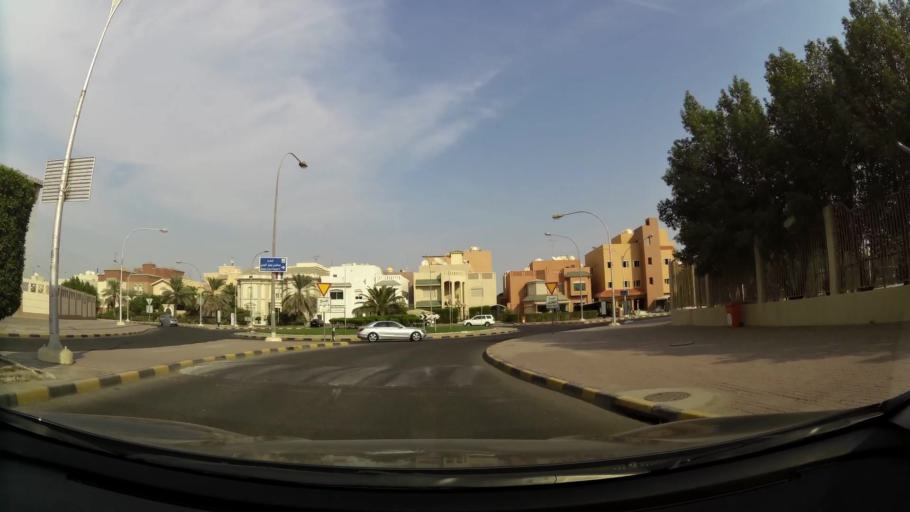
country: KW
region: Al Farwaniyah
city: Janub as Surrah
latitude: 29.3102
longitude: 47.9882
